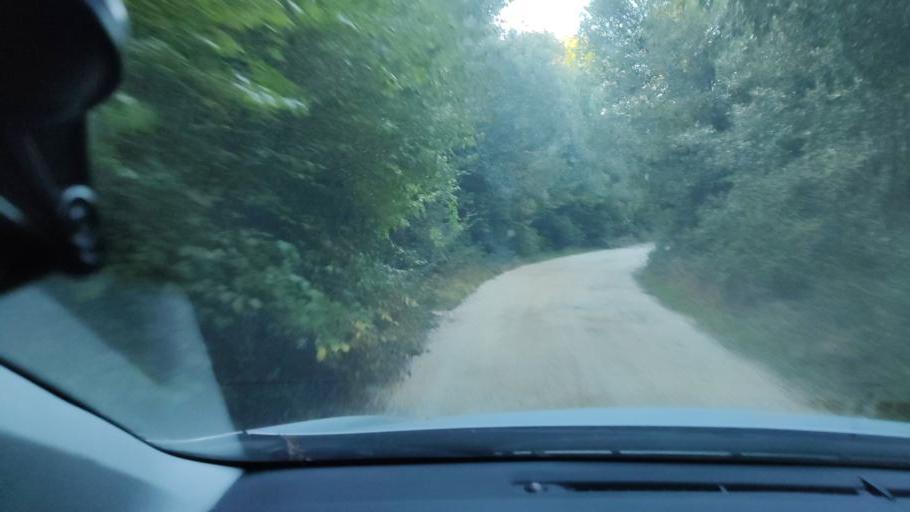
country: IT
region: Umbria
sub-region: Provincia di Terni
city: Amelia
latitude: 42.5820
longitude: 12.4342
